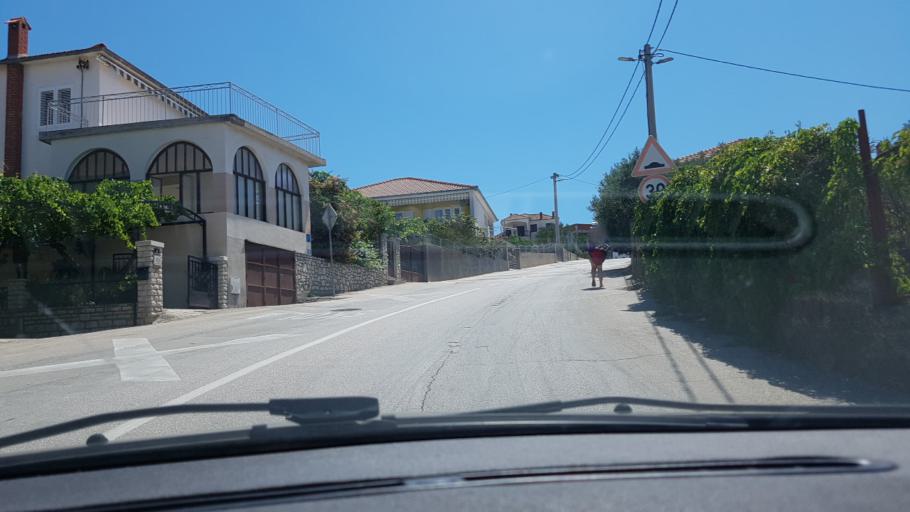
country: HR
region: Splitsko-Dalmatinska
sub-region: Grad Trogir
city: Trogir
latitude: 43.4955
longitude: 16.2627
